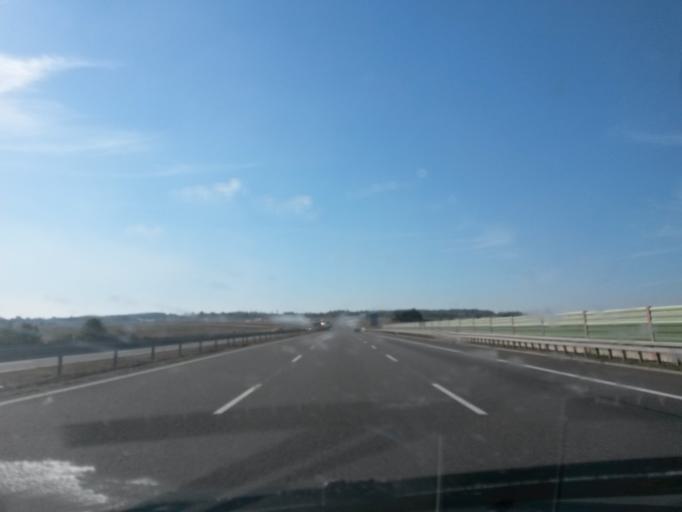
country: PL
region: Opole Voivodeship
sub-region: Powiat strzelecki
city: Lesnica
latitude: 50.4668
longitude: 18.1885
